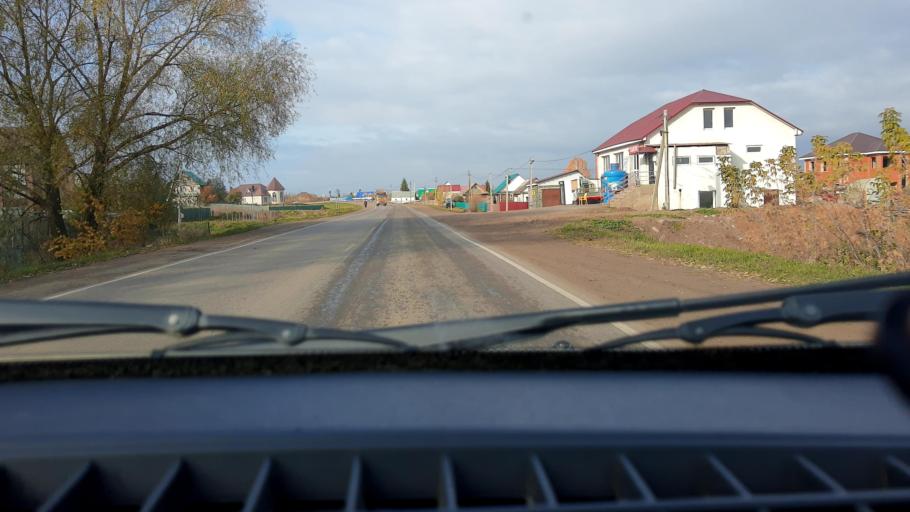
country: RU
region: Bashkortostan
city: Kabakovo
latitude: 54.5484
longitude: 56.0992
